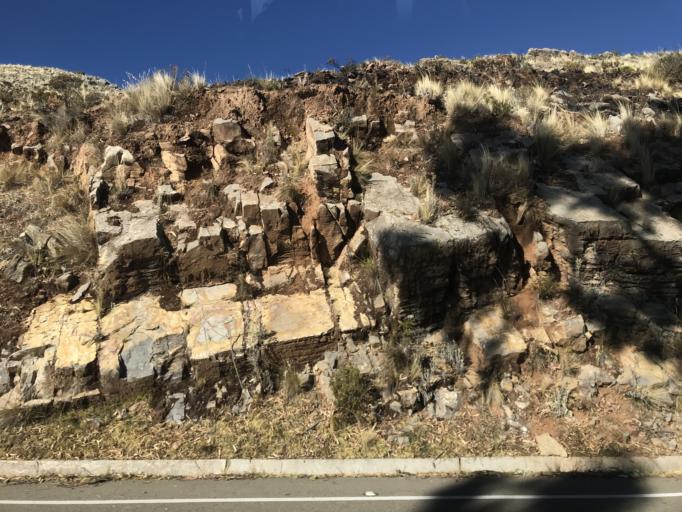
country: BO
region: La Paz
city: San Pedro
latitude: -16.1911
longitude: -68.9225
